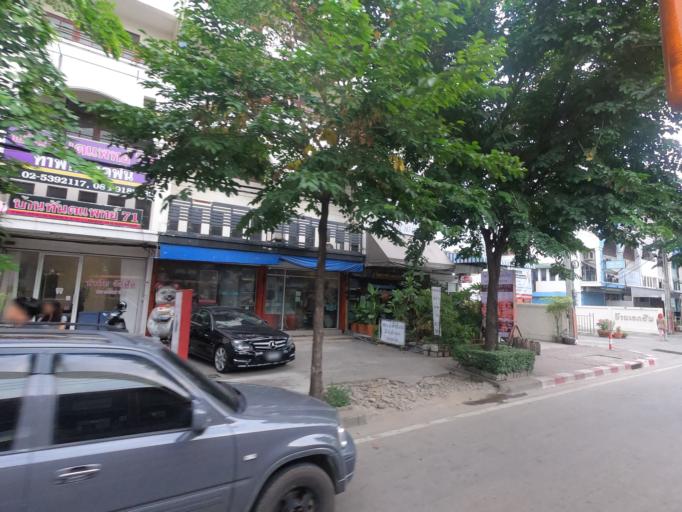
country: TH
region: Bangkok
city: Lat Phrao
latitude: 13.8187
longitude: 100.6096
